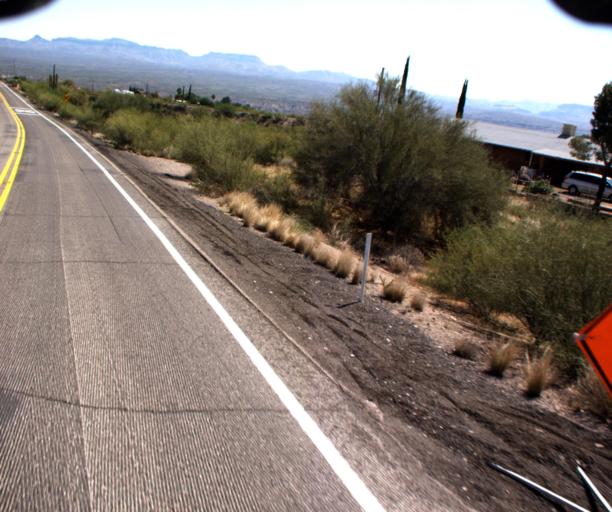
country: US
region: Arizona
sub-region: Pinal County
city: Mammoth
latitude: 32.6924
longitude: -110.6467
